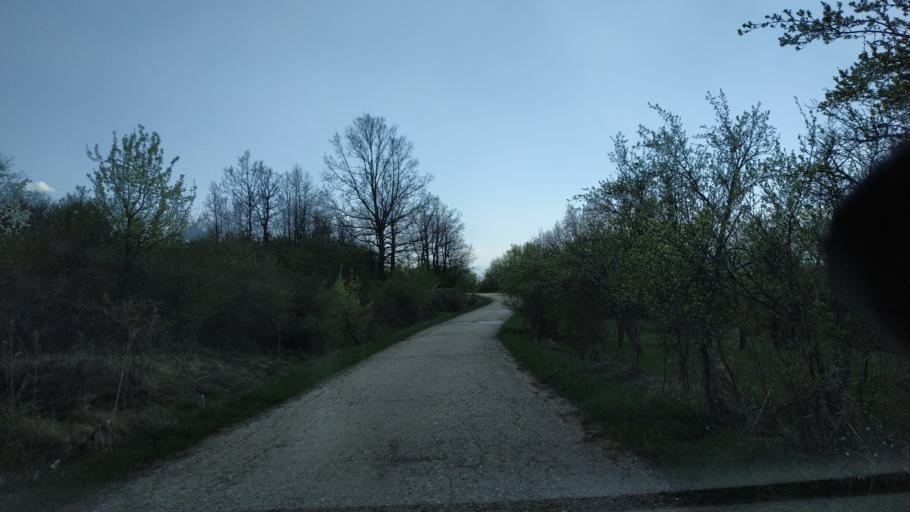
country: RS
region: Central Serbia
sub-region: Zajecarski Okrug
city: Soko Banja
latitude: 43.5634
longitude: 21.8953
